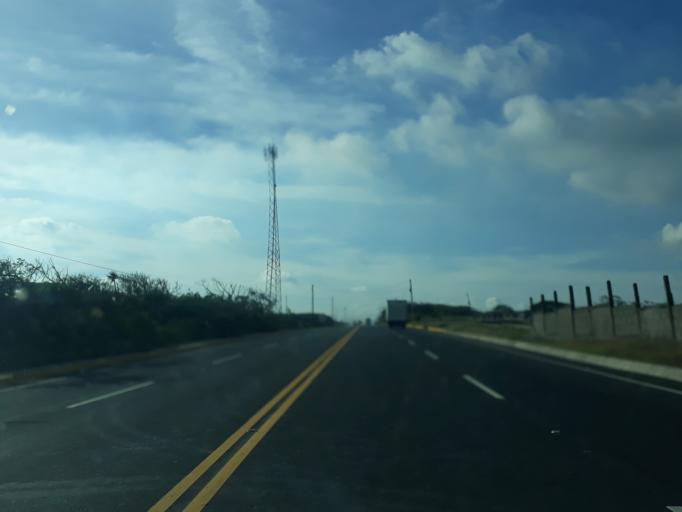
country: NI
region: Managua
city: El Crucero
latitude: 11.9249
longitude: -86.2829
